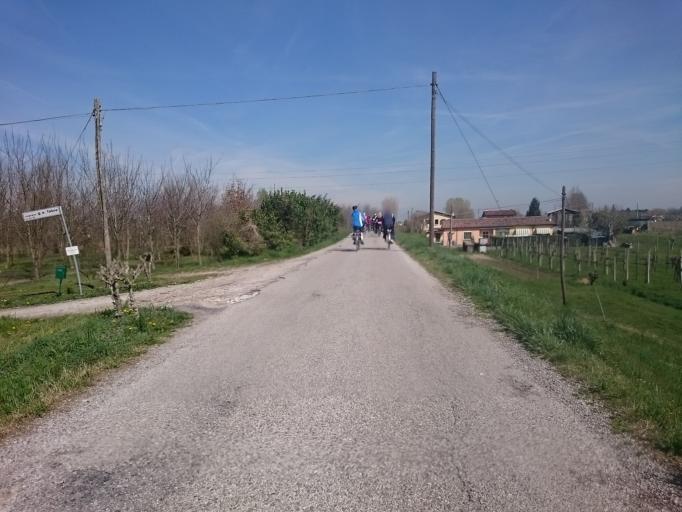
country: IT
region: Veneto
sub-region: Provincia di Padova
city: Sarmeola
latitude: 45.4290
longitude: 11.8291
